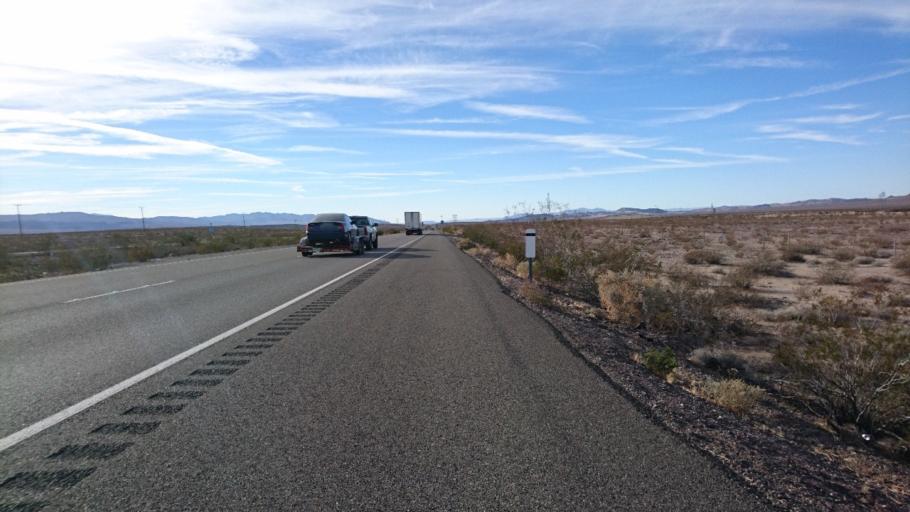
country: US
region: California
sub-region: San Bernardino County
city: Fort Irwin
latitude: 34.7745
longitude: -116.3752
